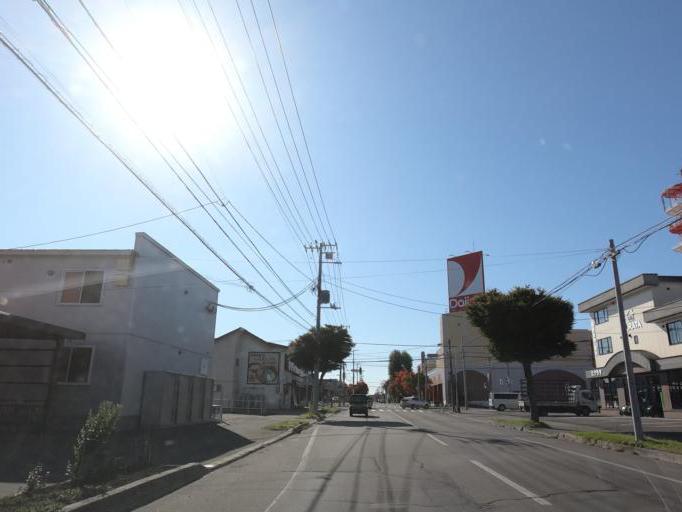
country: JP
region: Hokkaido
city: Obihiro
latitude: 42.9206
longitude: 143.2116
